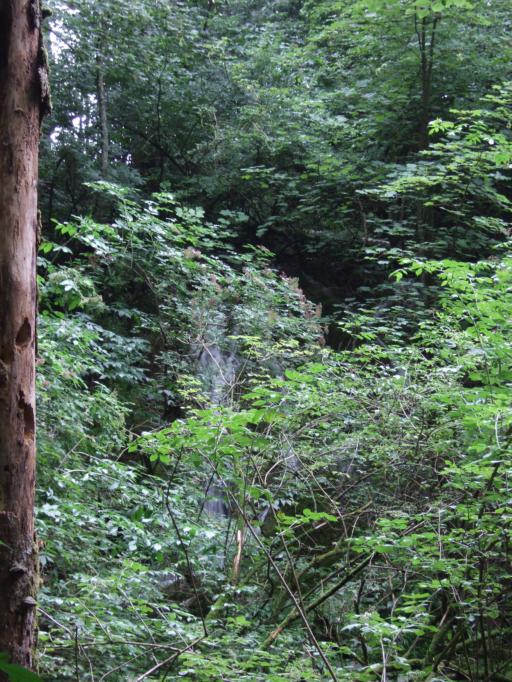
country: HR
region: Licko-Senjska
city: Jezerce
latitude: 44.8715
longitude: 15.6051
